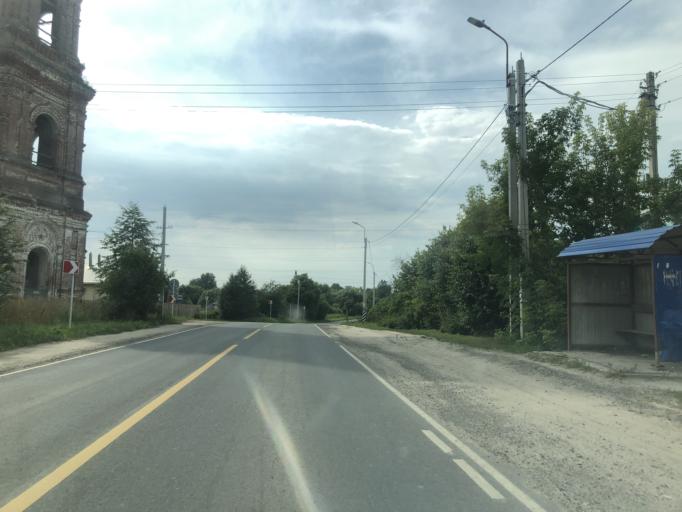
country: RU
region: Ivanovo
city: Shuya
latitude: 56.8541
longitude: 41.5475
